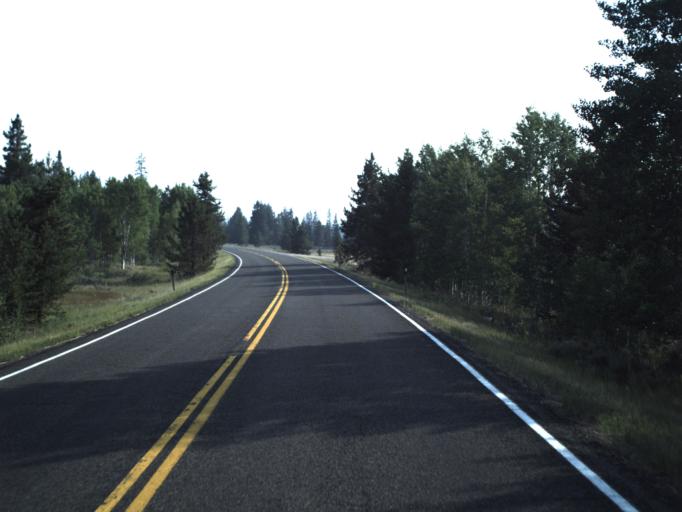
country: US
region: Wyoming
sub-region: Uinta County
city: Evanston
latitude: 40.8926
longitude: -110.8312
